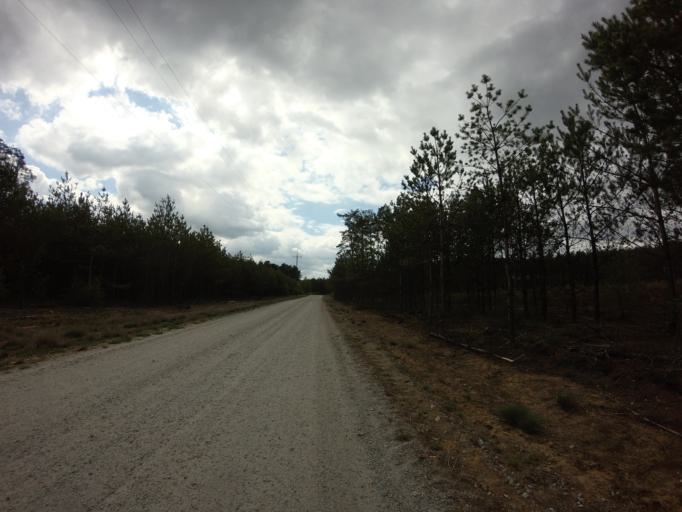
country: PL
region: West Pomeranian Voivodeship
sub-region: Powiat drawski
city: Kalisz Pomorski
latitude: 53.1940
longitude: 15.9741
